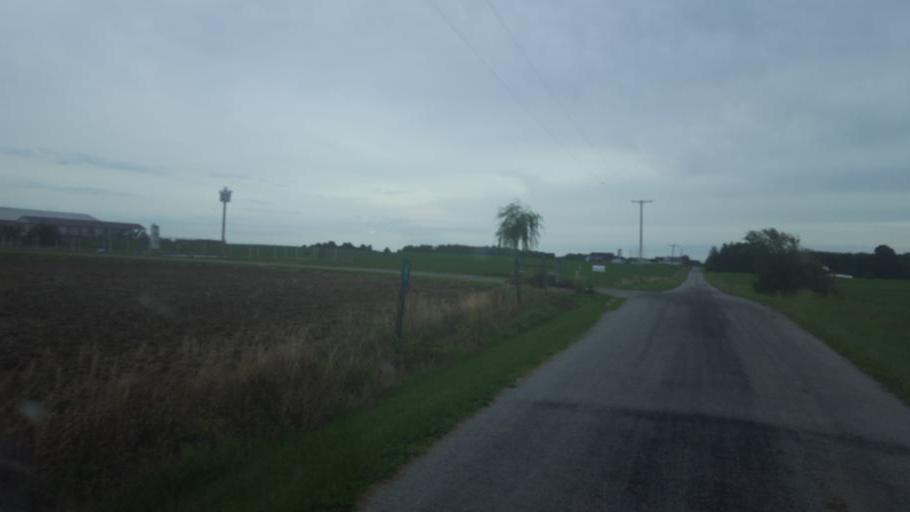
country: US
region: Ohio
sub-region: Huron County
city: Greenwich
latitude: 40.9240
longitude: -82.4906
